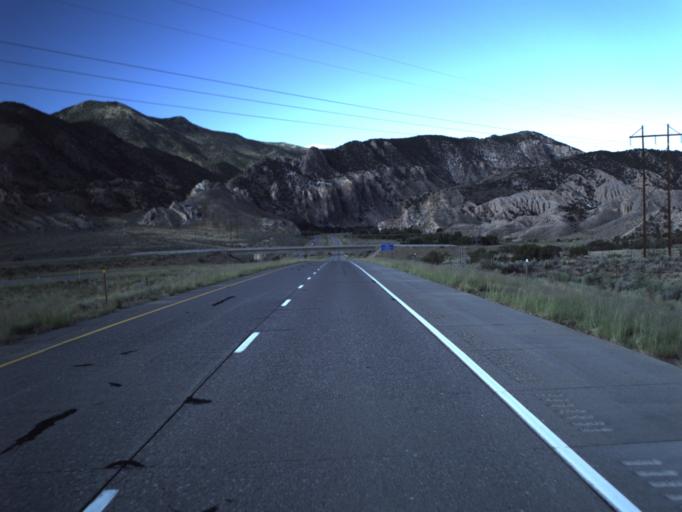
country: US
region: Utah
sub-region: Sevier County
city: Monroe
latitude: 38.5934
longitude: -112.2667
